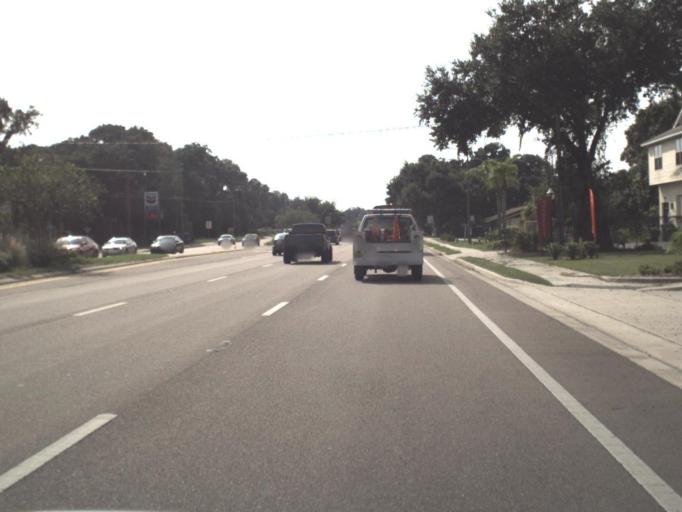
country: US
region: Florida
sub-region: Manatee County
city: Samoset
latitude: 27.4964
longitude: -82.5402
